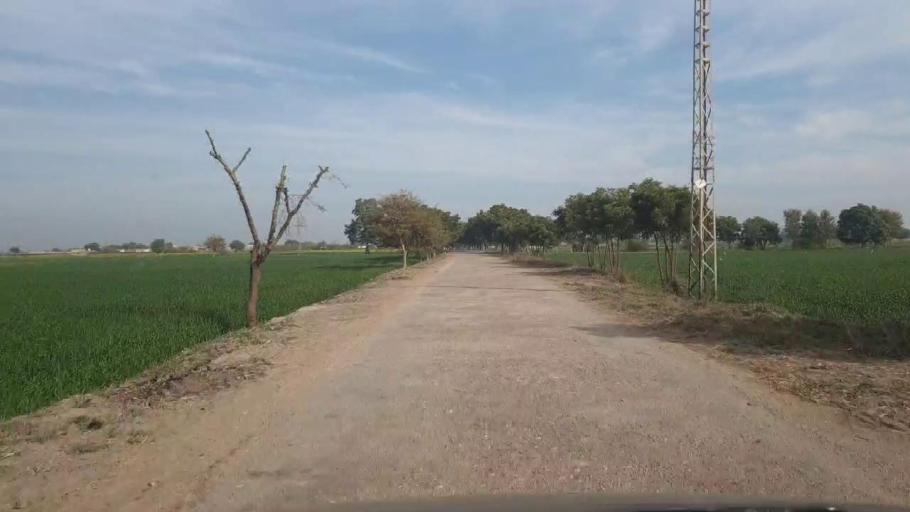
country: PK
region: Sindh
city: Khadro
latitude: 26.1538
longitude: 68.6949
